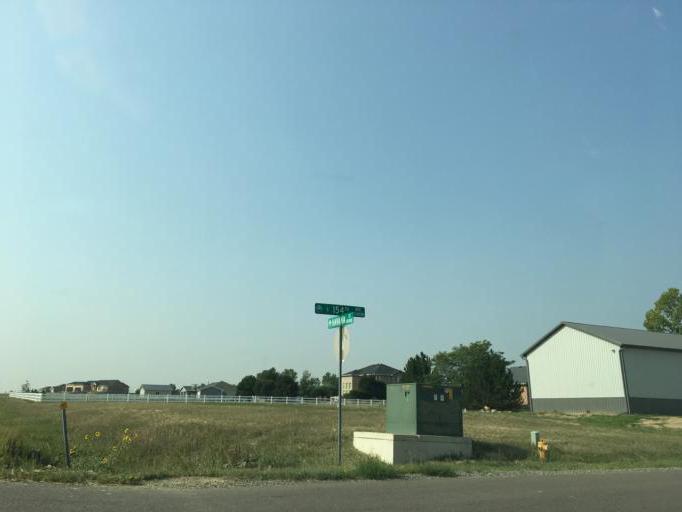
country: US
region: Colorado
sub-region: Adams County
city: Todd Creek
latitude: 39.9757
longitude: -104.8655
